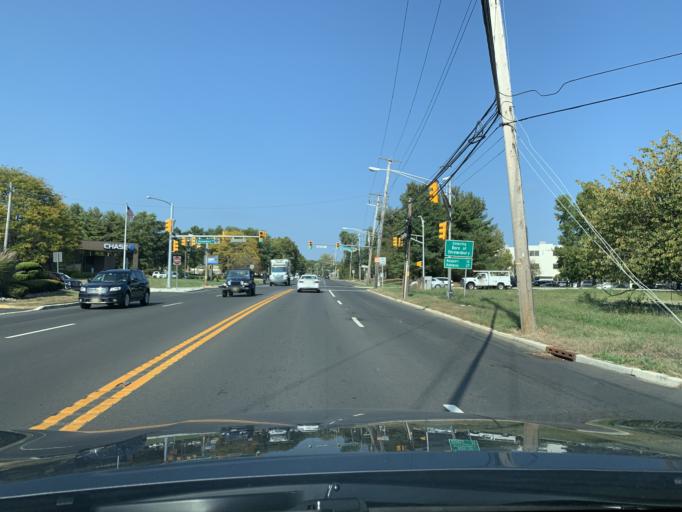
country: US
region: New Jersey
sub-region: Monmouth County
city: Shrewsbury
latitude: 40.3123
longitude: -74.0643
